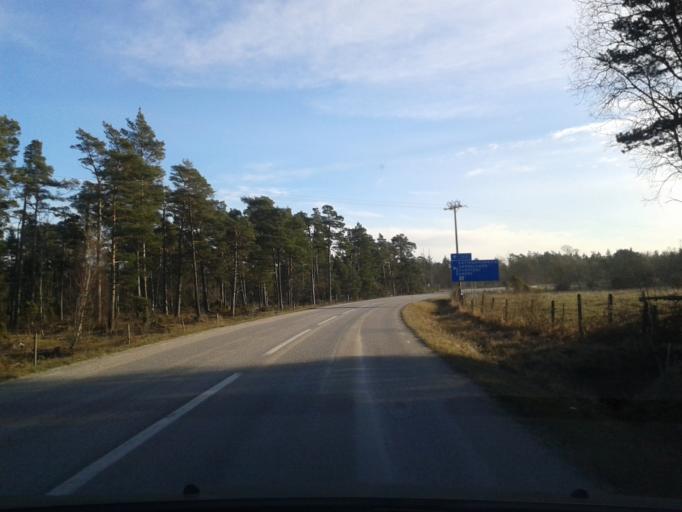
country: SE
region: Gotland
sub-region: Gotland
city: Hemse
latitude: 57.3630
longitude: 18.6822
